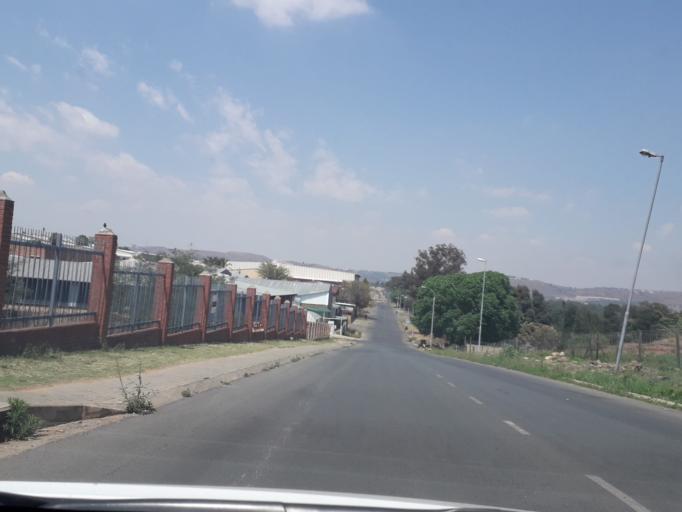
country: ZA
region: Gauteng
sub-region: West Rand District Municipality
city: Muldersdriseloop
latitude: -26.0771
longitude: 27.9125
